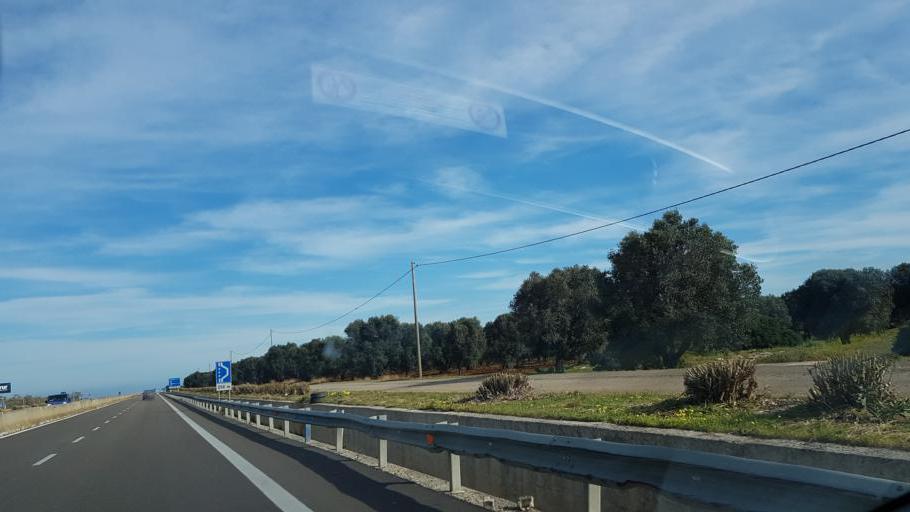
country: IT
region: Apulia
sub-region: Provincia di Brindisi
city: San Vito dei Normanni
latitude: 40.7196
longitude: 17.7547
